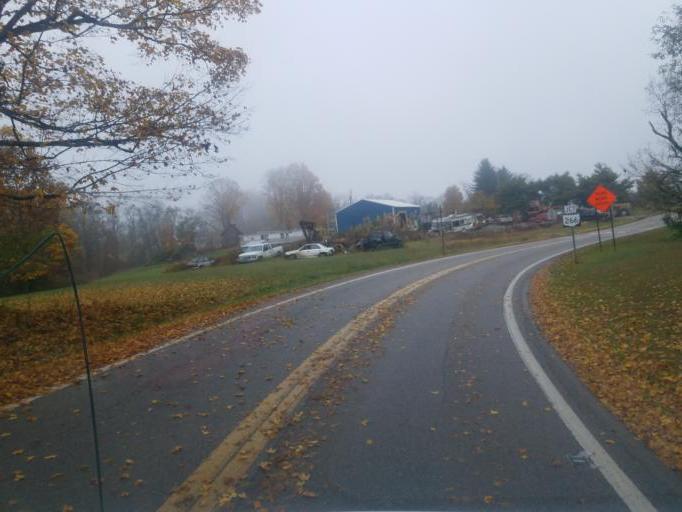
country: US
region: Ohio
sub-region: Morgan County
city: McConnelsville
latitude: 39.5468
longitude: -81.8181
